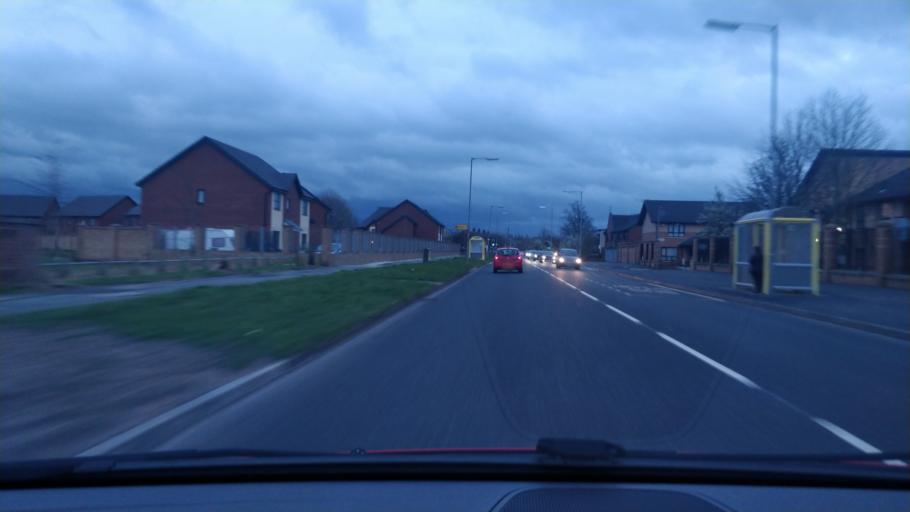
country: GB
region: England
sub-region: Knowsley
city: Kirkby
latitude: 53.4543
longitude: -2.9060
